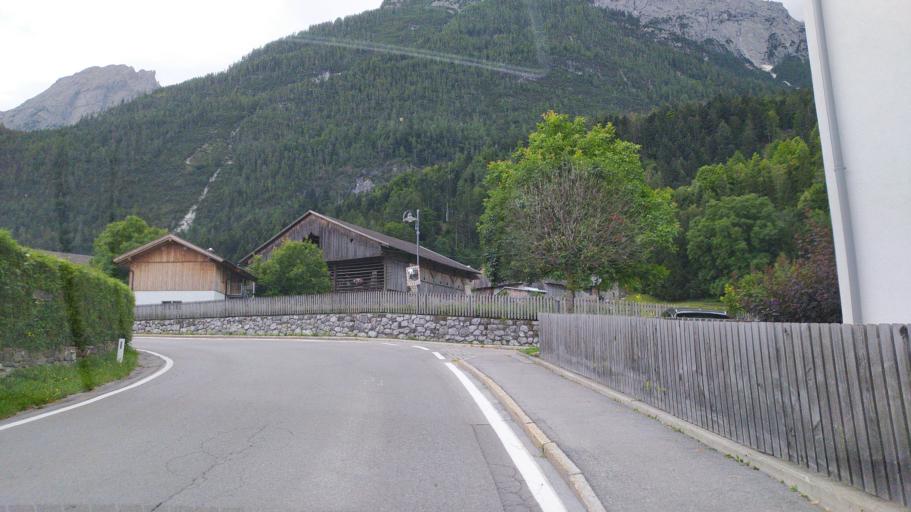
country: AT
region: Tyrol
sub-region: Politischer Bezirk Lienz
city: Lavant
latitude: 46.7977
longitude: 12.8395
